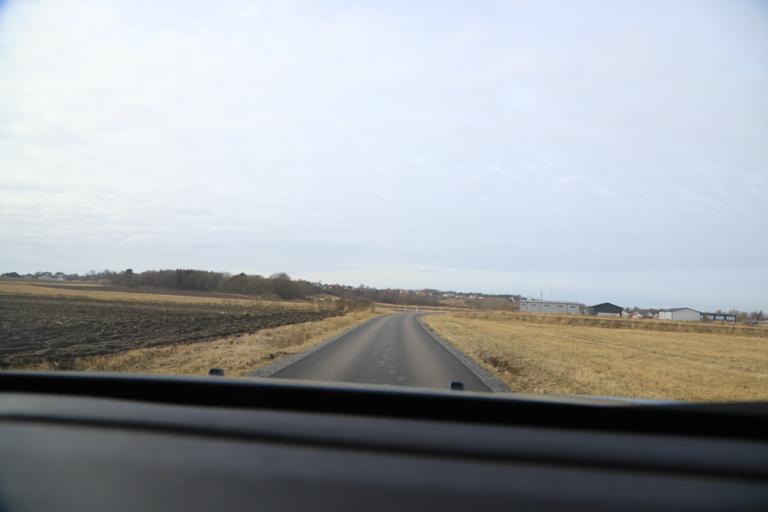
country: SE
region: Halland
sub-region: Kungsbacka Kommun
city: Frillesas
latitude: 57.2328
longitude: 12.1396
